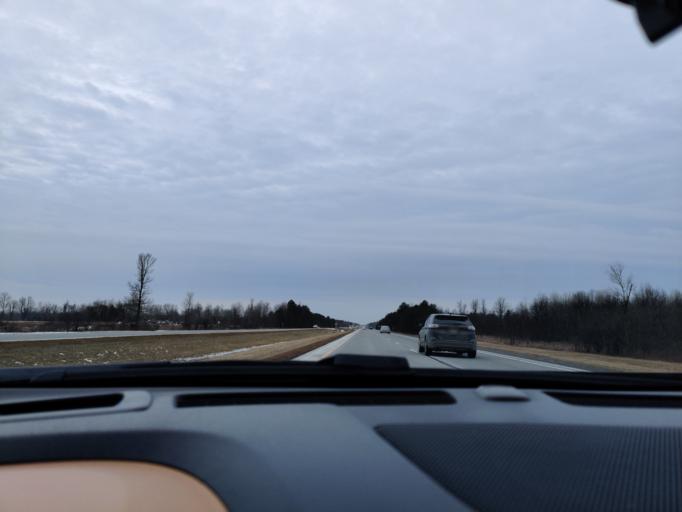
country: US
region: New York
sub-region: St. Lawrence County
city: Ogdensburg
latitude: 44.8361
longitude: -75.3649
